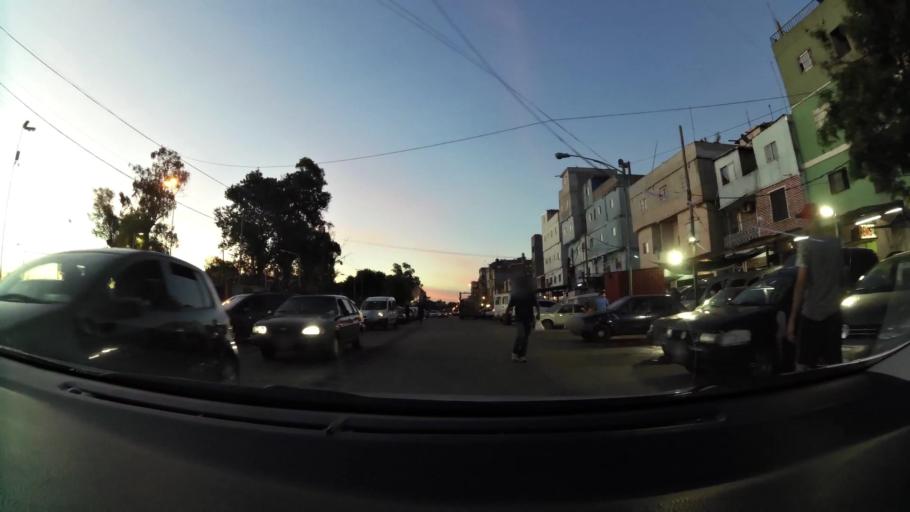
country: AR
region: Buenos Aires F.D.
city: Villa Lugano
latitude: -34.6507
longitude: -58.4450
